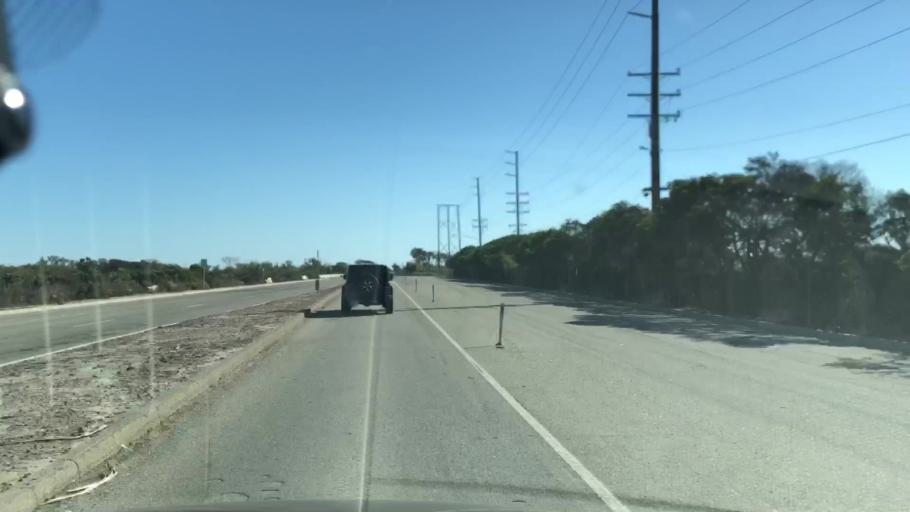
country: US
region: California
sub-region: Ventura County
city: Oxnard Shores
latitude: 34.2388
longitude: -119.2567
